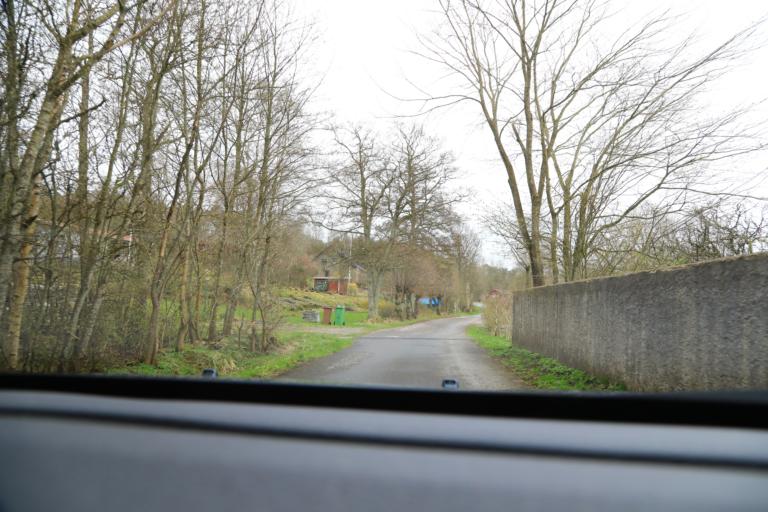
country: SE
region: Halland
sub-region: Kungsbacka Kommun
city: Frillesas
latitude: 57.3101
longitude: 12.1802
